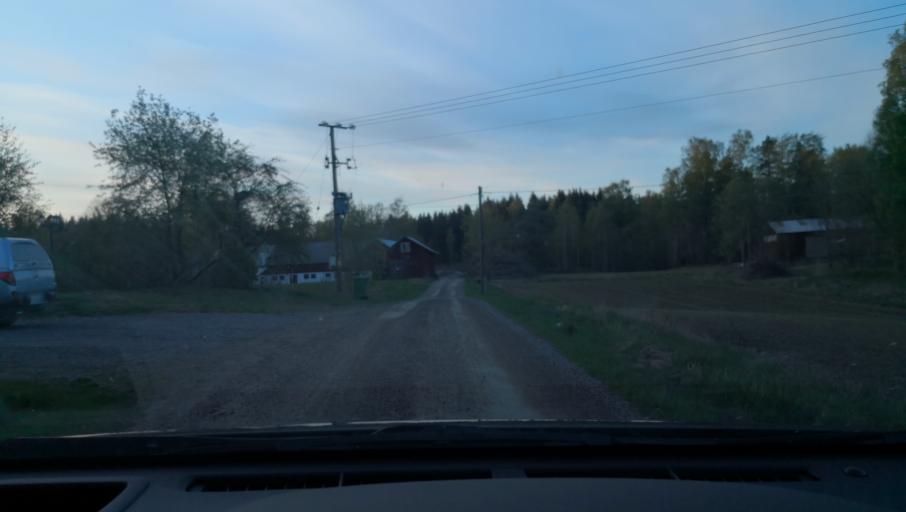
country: SE
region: OErebro
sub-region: Askersunds Kommun
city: Askersund
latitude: 58.9742
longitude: 14.9458
